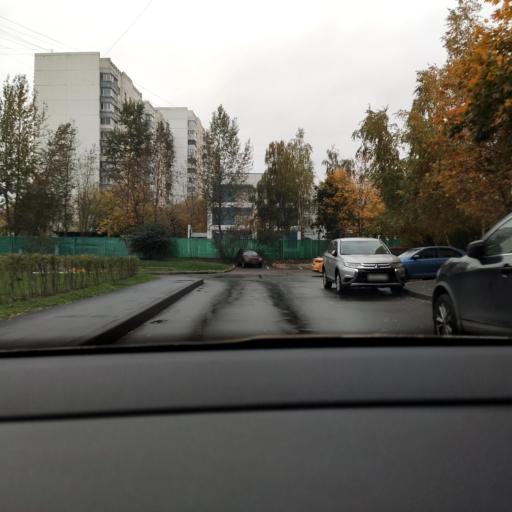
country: RU
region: Moscow
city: Zhulebino
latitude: 55.7011
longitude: 37.8430
